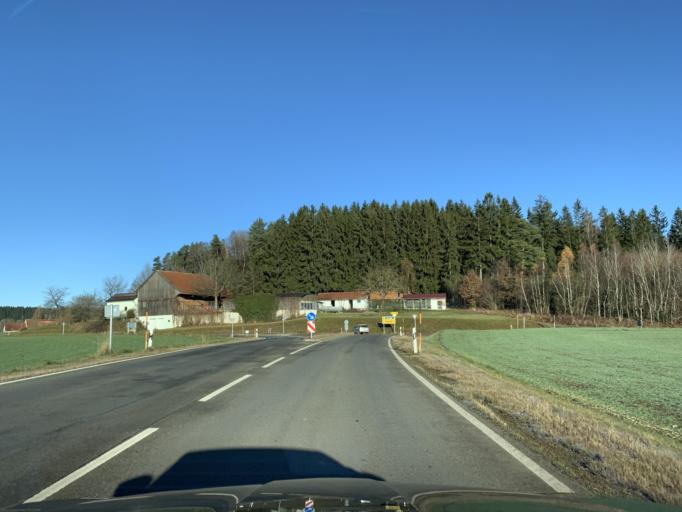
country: DE
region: Bavaria
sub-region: Upper Palatinate
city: Winklarn
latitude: 49.4671
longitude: 12.4627
